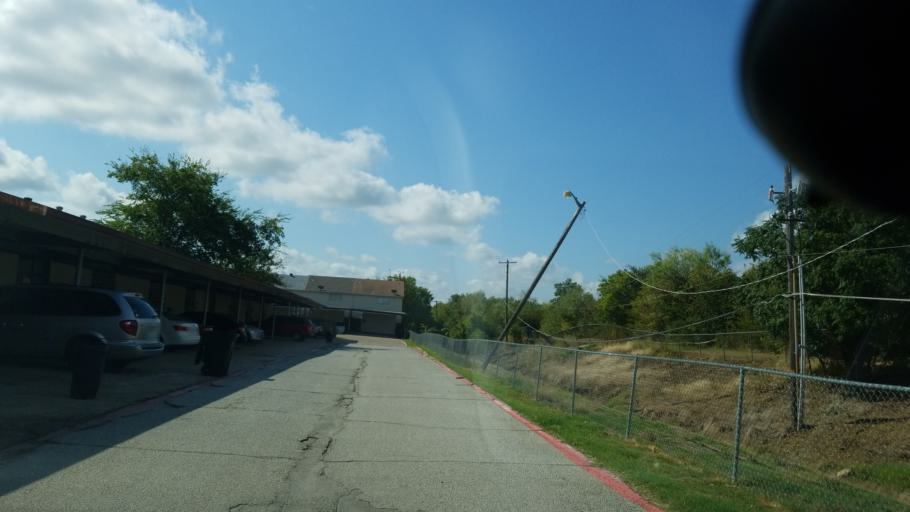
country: US
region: Texas
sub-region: Dallas County
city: Grand Prairie
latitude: 32.6966
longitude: -96.9910
